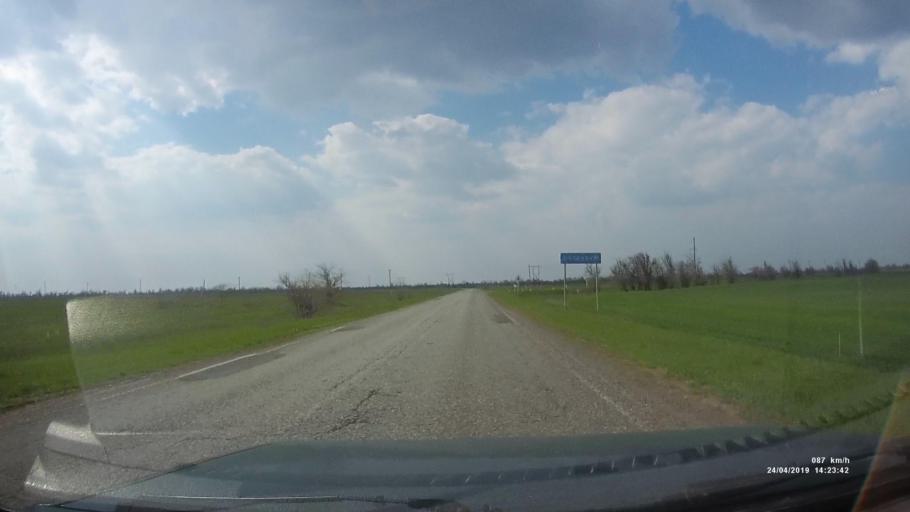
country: RU
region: Kalmykiya
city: Arshan'
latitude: 46.3244
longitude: 44.1105
